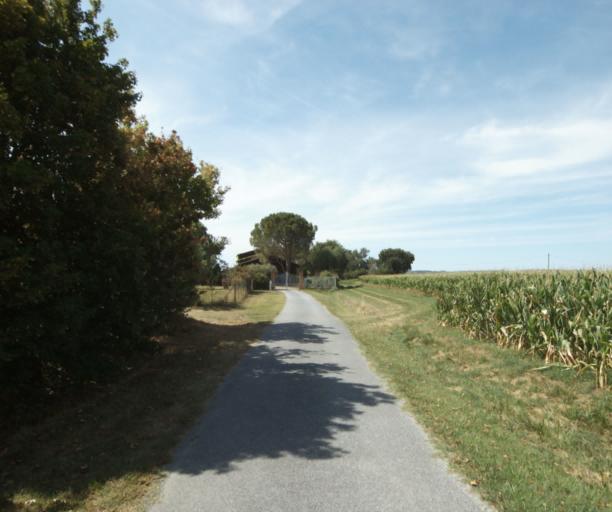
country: FR
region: Midi-Pyrenees
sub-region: Departement de la Haute-Garonne
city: Revel
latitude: 43.5068
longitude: 2.0298
